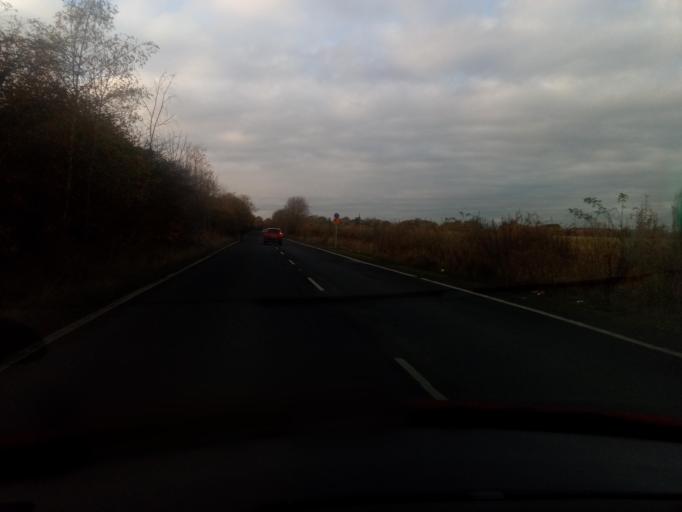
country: GB
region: England
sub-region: City and Borough of Leeds
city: Wetherby
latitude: 53.9401
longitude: -1.3814
